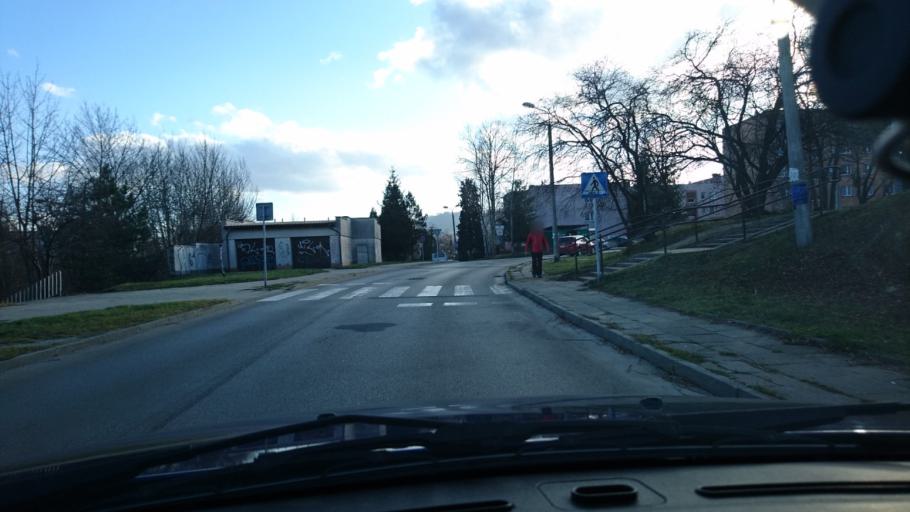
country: PL
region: Silesian Voivodeship
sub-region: Bielsko-Biala
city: Bielsko-Biala
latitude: 49.8085
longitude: 19.0280
